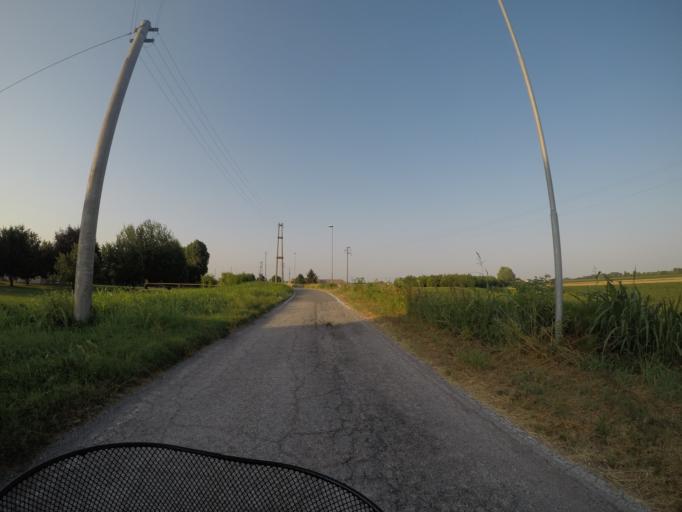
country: IT
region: Veneto
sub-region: Provincia di Rovigo
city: Fratta Polesine
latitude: 45.0109
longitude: 11.6415
